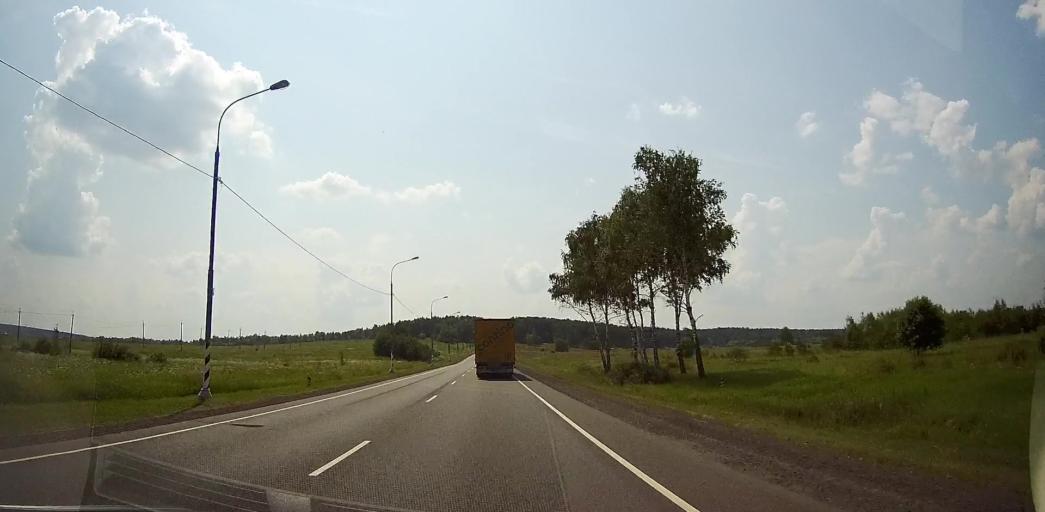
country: RU
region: Moskovskaya
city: Meshcherino
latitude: 55.1862
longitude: 38.3562
